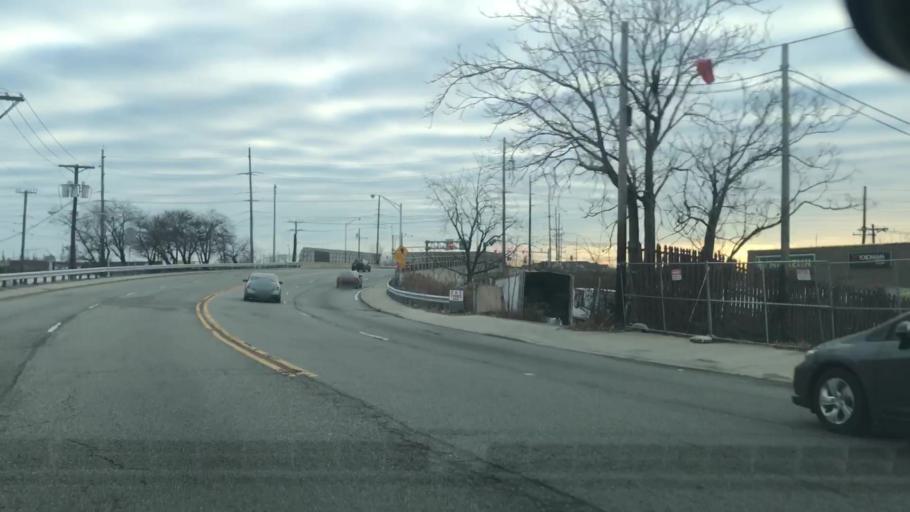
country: US
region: New Jersey
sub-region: Bergen County
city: East Rutherford
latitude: 40.8333
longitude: -74.0902
